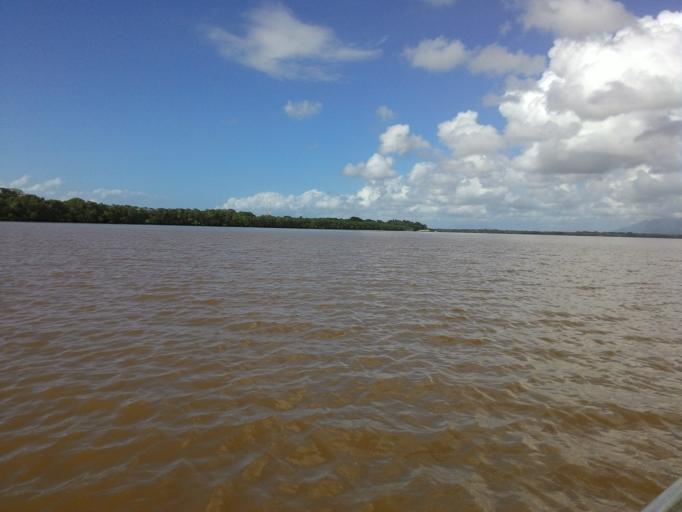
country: BR
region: Sao Paulo
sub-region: Cananeia
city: Cananeia
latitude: -24.8833
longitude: -47.7923
